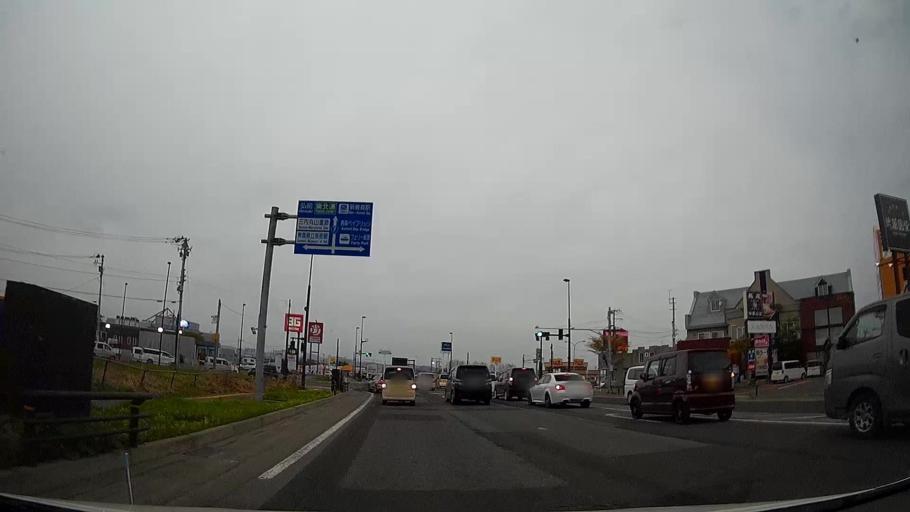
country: JP
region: Aomori
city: Aomori Shi
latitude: 40.8320
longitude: 140.7019
